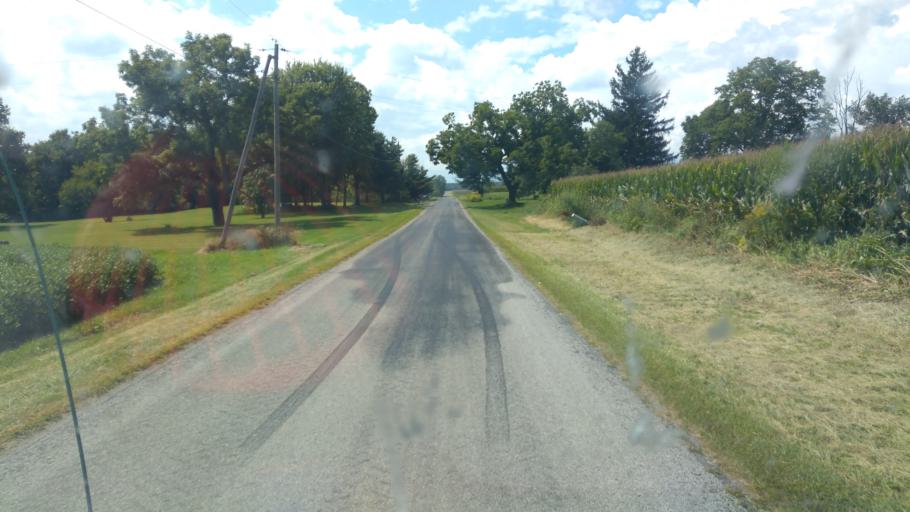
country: US
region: Ohio
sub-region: Union County
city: Richwood
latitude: 40.6001
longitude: -83.3882
